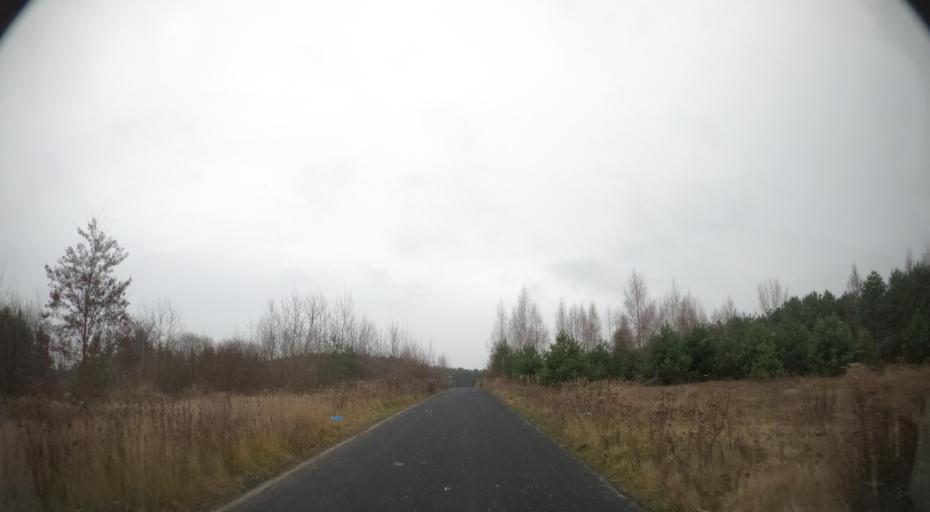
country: PL
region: Masovian Voivodeship
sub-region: Powiat radomski
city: Jedlnia-Letnisko
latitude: 51.4013
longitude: 21.2789
